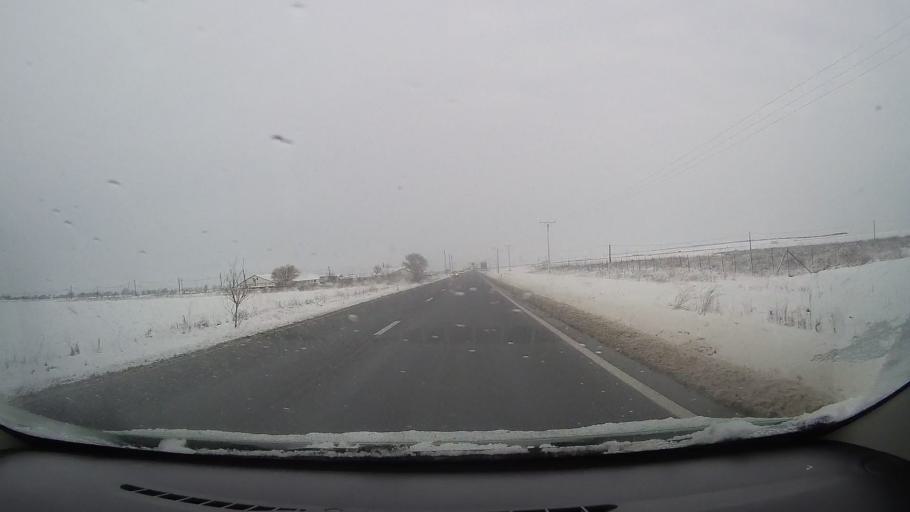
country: RO
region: Alba
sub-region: Municipiul Sebes
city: Lancram
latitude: 45.9685
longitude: 23.5285
